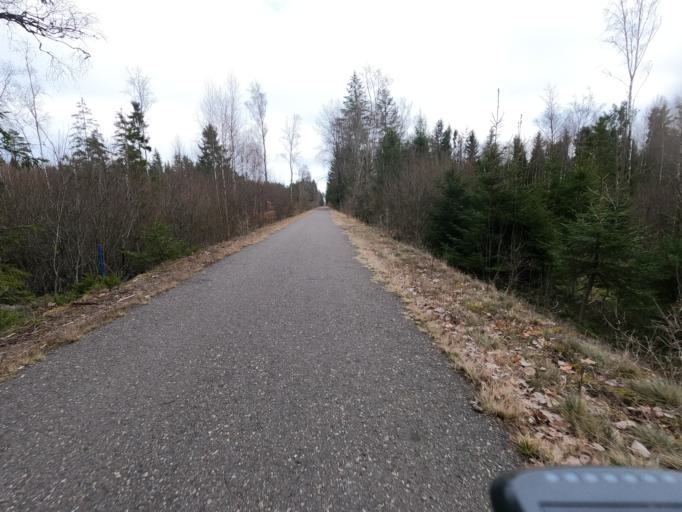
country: SE
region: Joenkoeping
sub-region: Varnamo Kommun
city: Rydaholm
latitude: 56.8465
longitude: 14.2137
